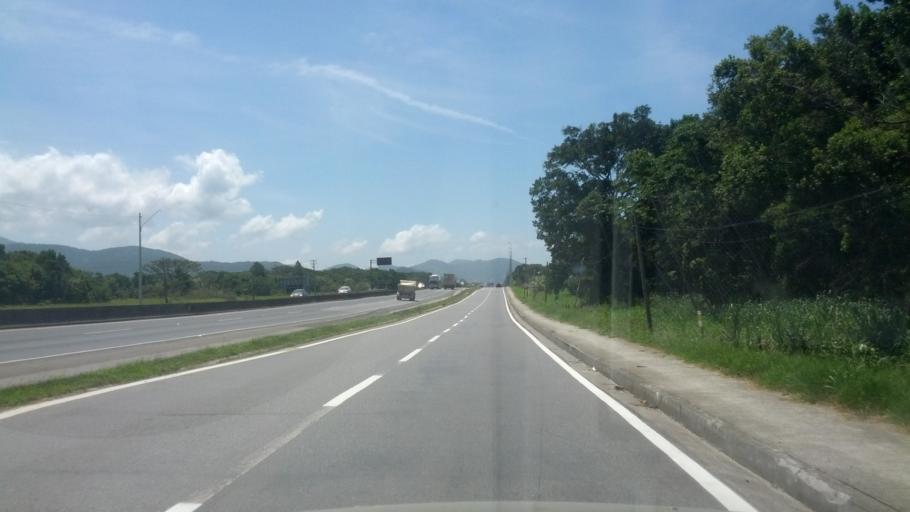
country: BR
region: Santa Catarina
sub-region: Porto Belo
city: Porto Belo
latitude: -27.1612
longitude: -48.6109
